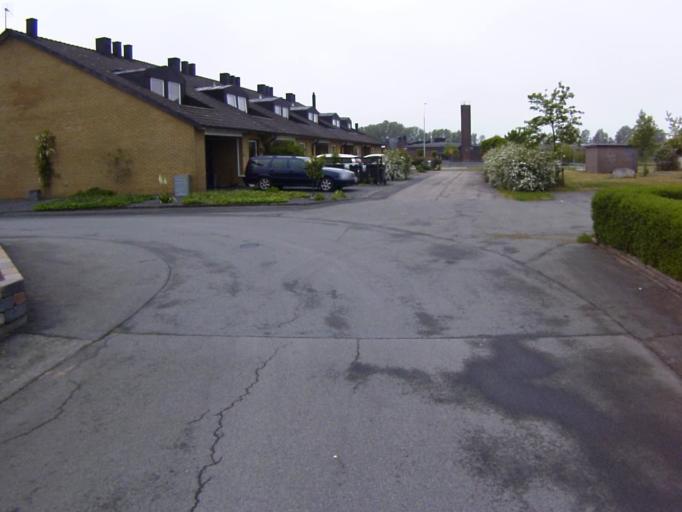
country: SE
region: Skane
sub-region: Kristianstads Kommun
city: Ahus
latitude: 55.9257
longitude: 14.2876
